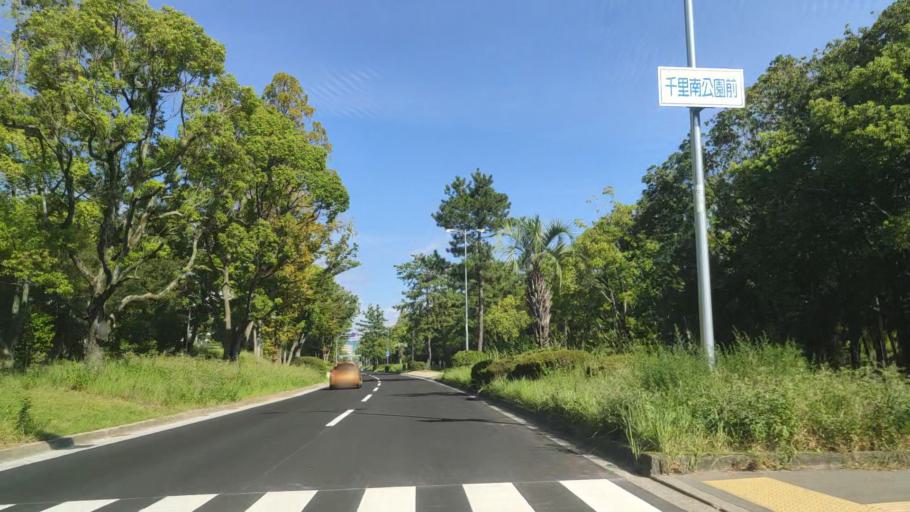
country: JP
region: Osaka
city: Suita
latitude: 34.7944
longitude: 135.5075
